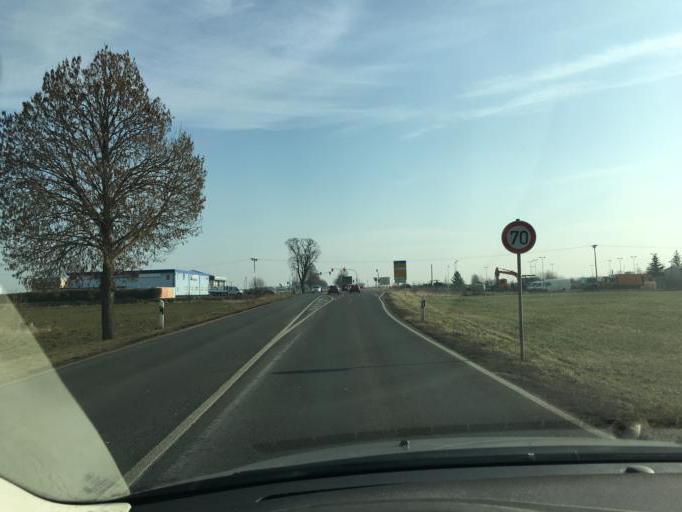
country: DE
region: Saxony-Anhalt
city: Dieskau
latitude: 51.4425
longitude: 12.0409
